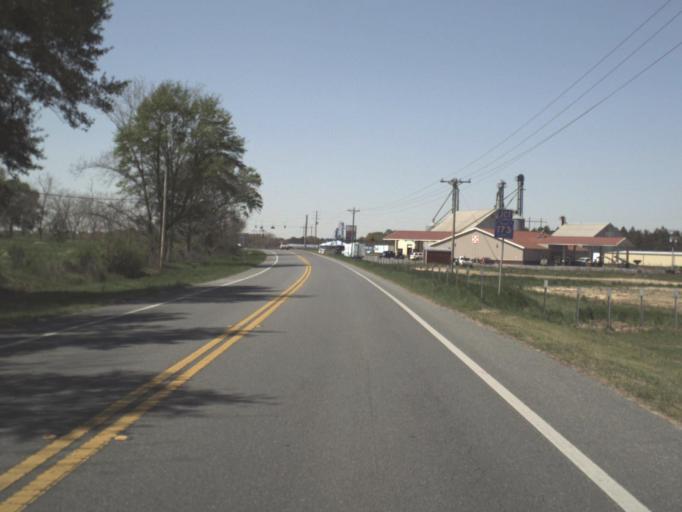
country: US
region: Florida
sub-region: Jackson County
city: Graceville
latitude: 30.9648
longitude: -85.5773
